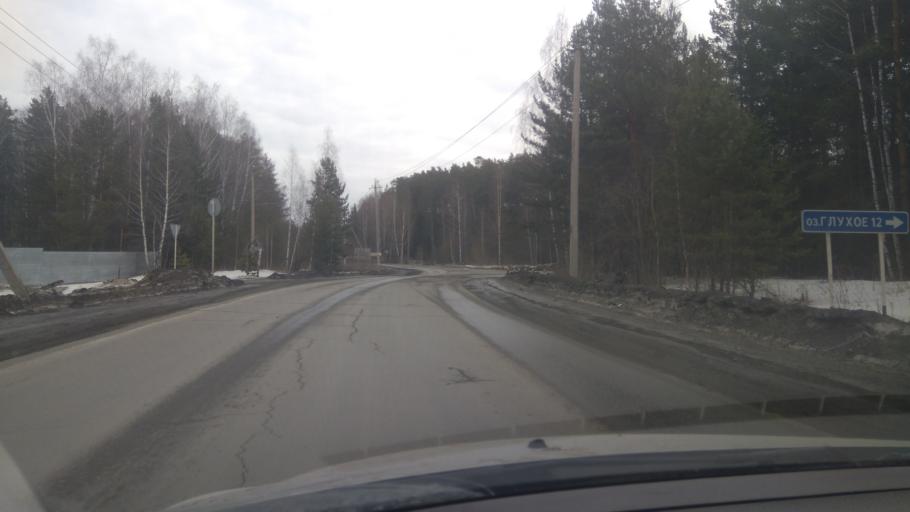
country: RU
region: Sverdlovsk
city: Severka
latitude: 56.8331
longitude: 60.3905
